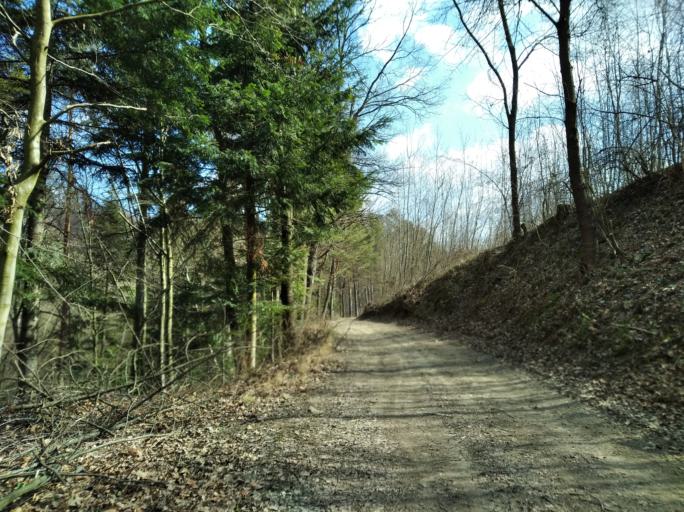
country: PL
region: Subcarpathian Voivodeship
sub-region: Powiat strzyzowski
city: Jawornik
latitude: 49.8440
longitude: 21.8413
